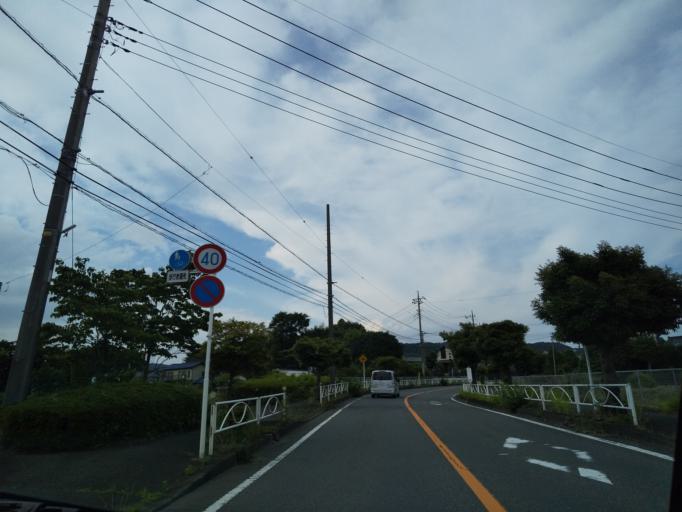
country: JP
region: Kanagawa
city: Atsugi
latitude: 35.4849
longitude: 139.3232
